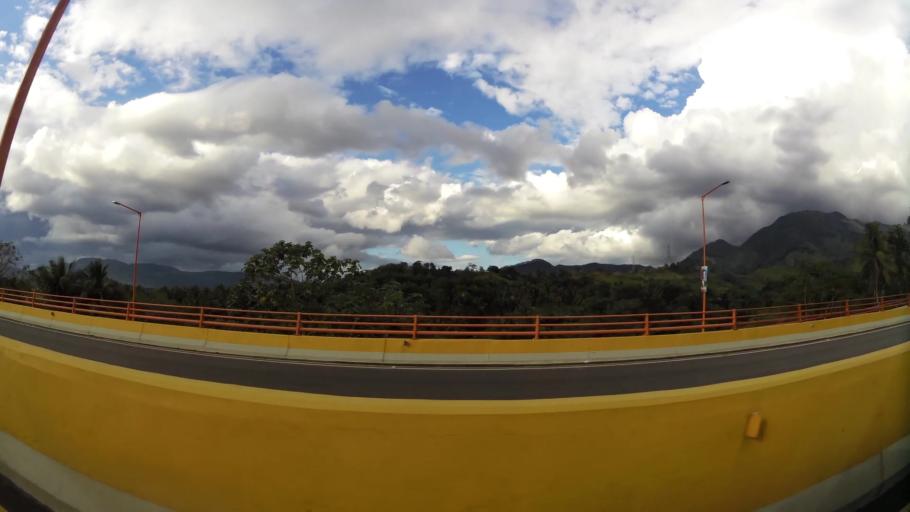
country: DO
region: Monsenor Nouel
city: Piedra Blanca
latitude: 18.8434
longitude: -70.3135
